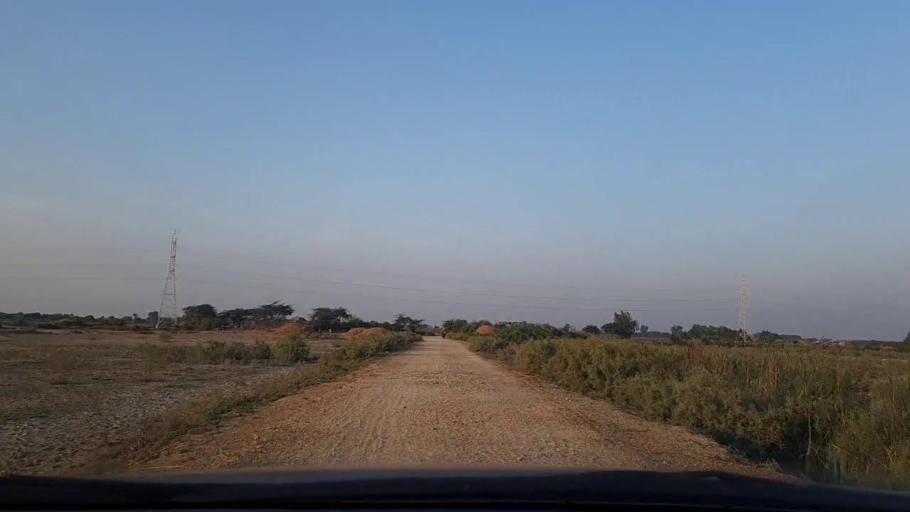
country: PK
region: Sindh
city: Mirpur Sakro
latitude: 24.5598
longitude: 67.6581
